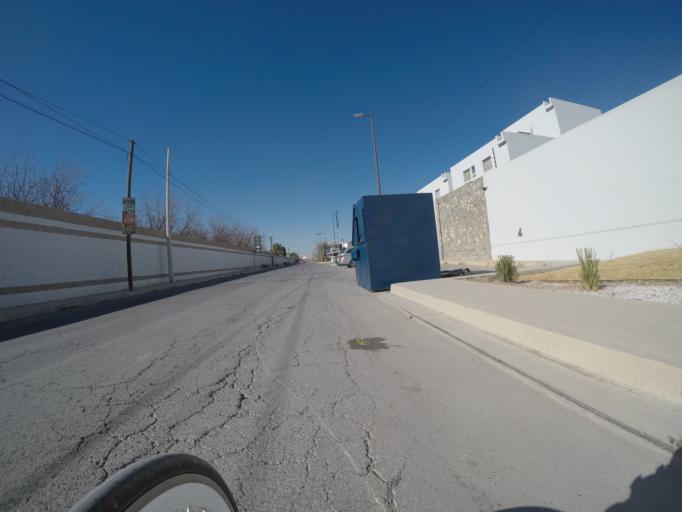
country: MX
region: Chihuahua
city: Ciudad Juarez
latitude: 31.6932
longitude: -106.3964
